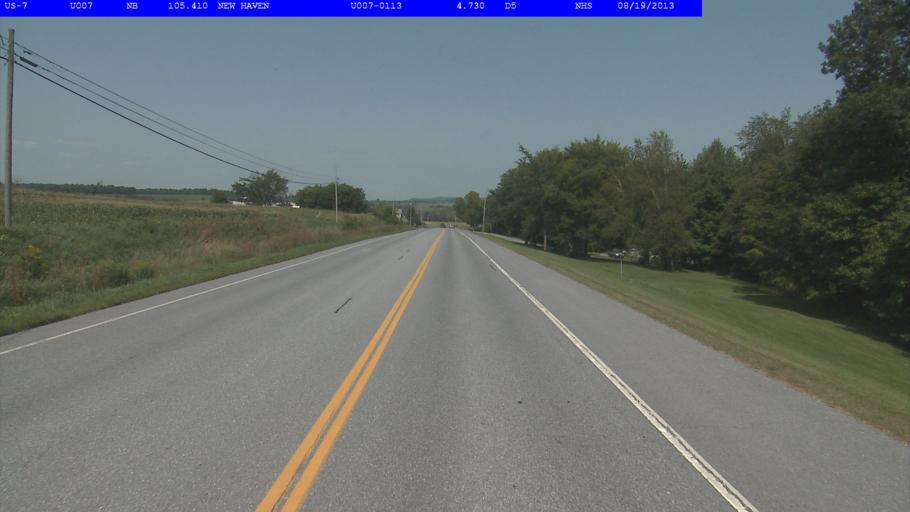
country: US
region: Vermont
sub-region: Addison County
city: Vergennes
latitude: 44.1135
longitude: -73.1755
